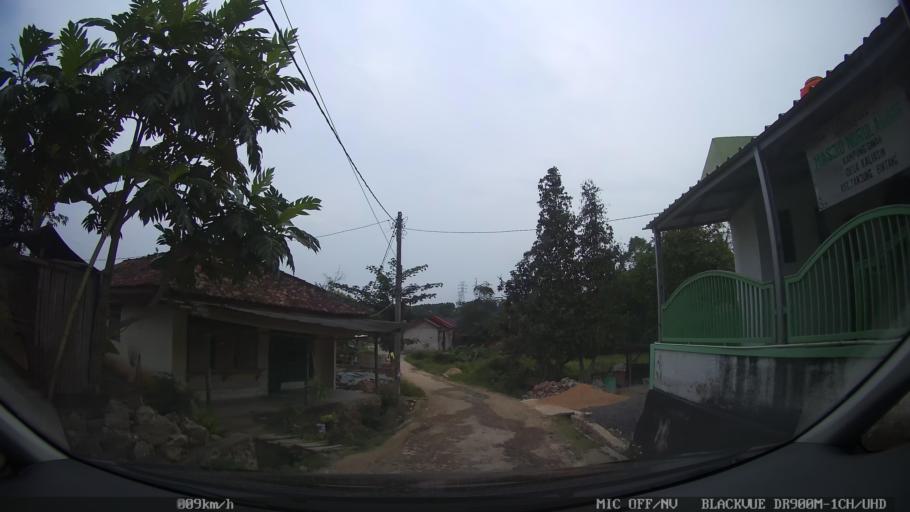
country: ID
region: Lampung
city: Panjang
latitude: -5.4271
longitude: 105.3411
